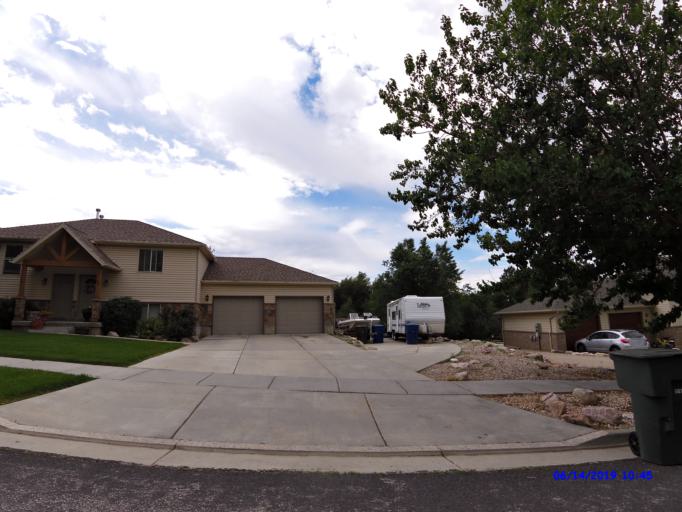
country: US
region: Utah
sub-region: Weber County
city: Ogden
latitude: 41.2416
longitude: -111.9405
